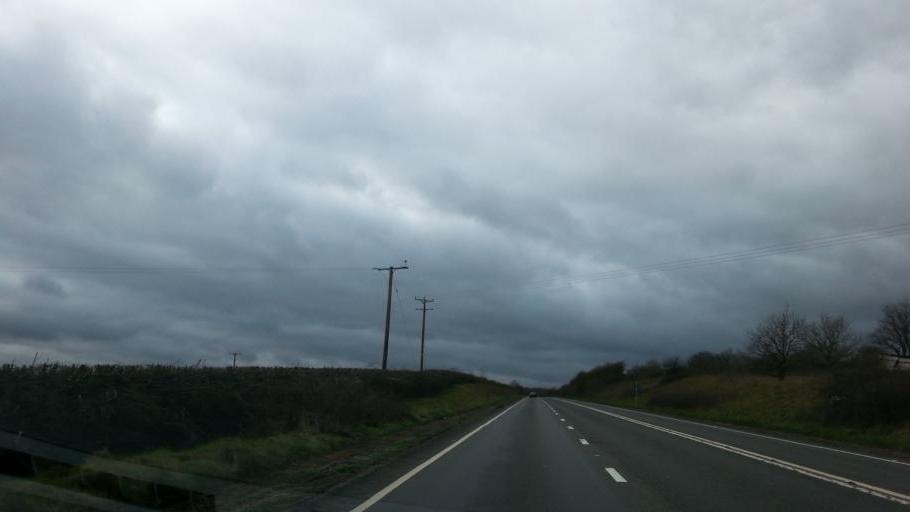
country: GB
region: England
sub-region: Devon
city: Tiverton
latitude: 50.9226
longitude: -3.5181
